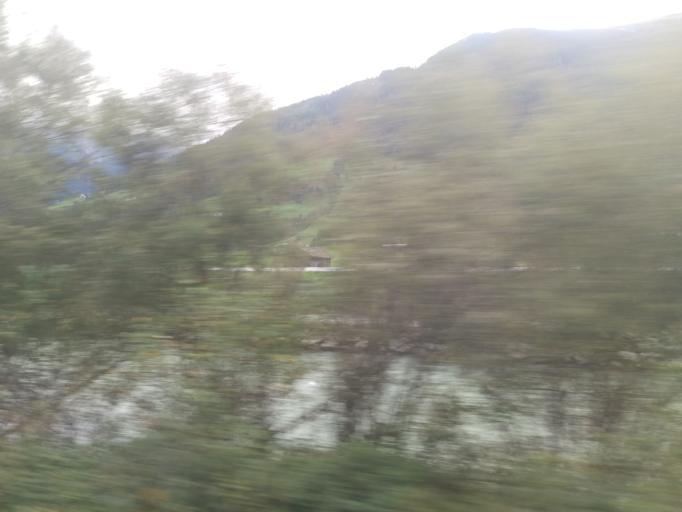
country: AT
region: Salzburg
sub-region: Politischer Bezirk Zell am See
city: Mittersill
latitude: 47.2837
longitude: 12.4576
